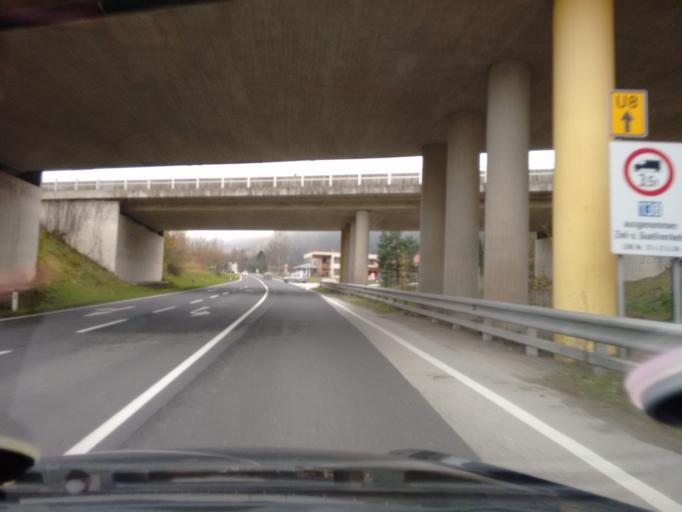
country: AT
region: Upper Austria
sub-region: Politischer Bezirk Kirchdorf an der Krems
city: Micheldorf in Oberoesterreich
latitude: 47.8447
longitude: 14.1700
